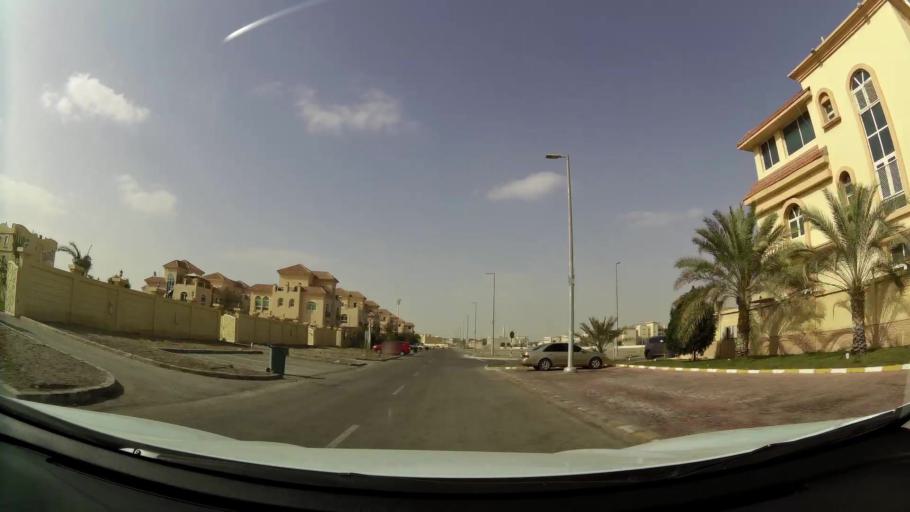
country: AE
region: Abu Dhabi
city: Abu Dhabi
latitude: 24.4173
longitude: 54.5958
